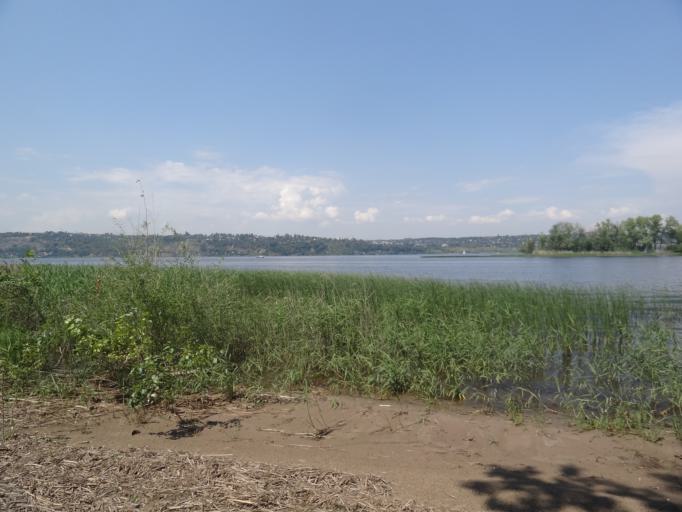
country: RU
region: Saratov
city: Engel's
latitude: 51.5483
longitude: 46.1173
